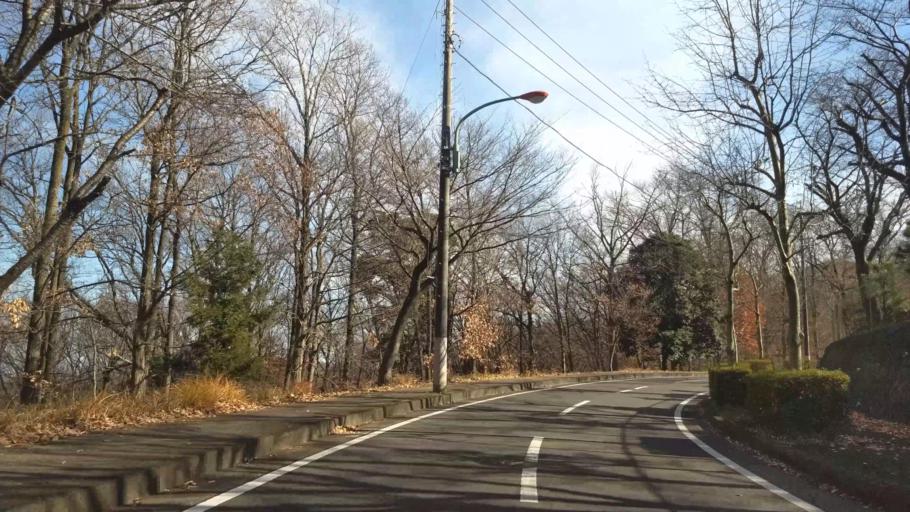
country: JP
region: Kanagawa
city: Hadano
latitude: 35.3567
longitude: 139.2284
